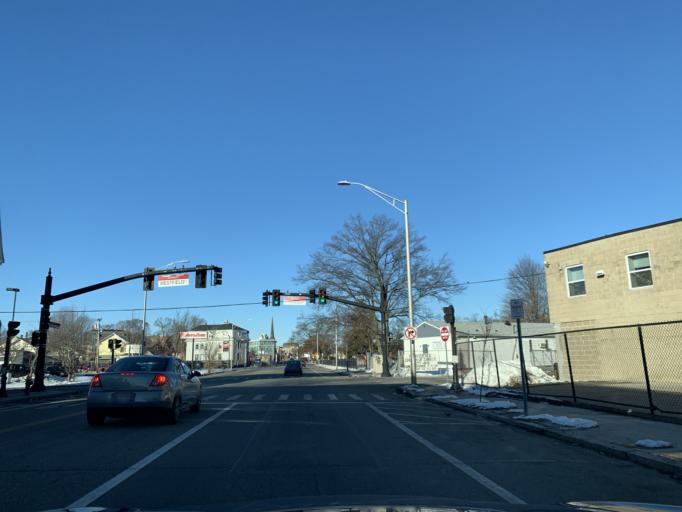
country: US
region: Rhode Island
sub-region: Providence County
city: Providence
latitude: 41.8096
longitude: -71.4242
